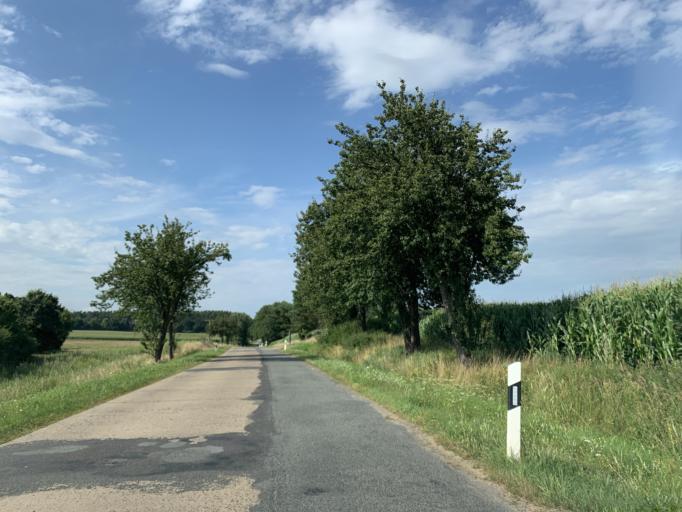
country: DE
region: Mecklenburg-Vorpommern
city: Carpin
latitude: 53.3682
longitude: 13.1781
